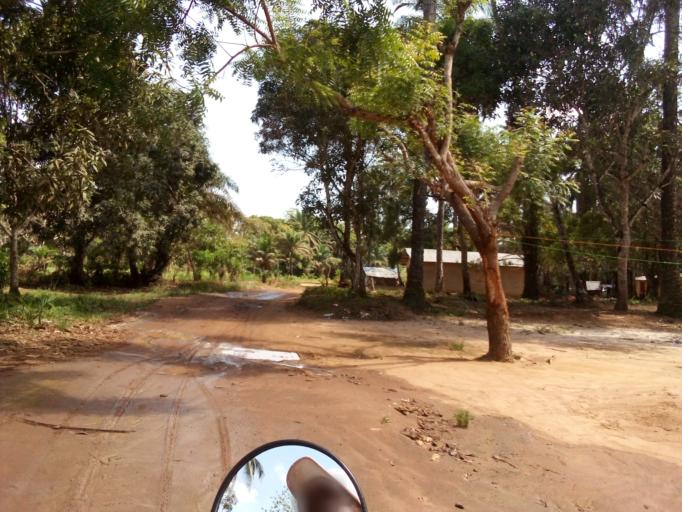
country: SL
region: Western Area
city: Waterloo
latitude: 8.3402
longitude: -13.0092
